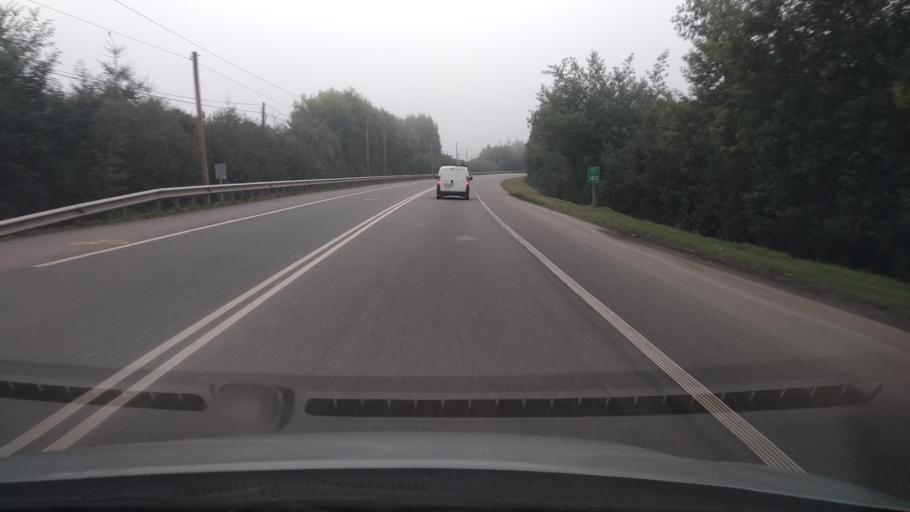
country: CL
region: Los Lagos
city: Las Animas
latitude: -39.7512
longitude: -73.2291
